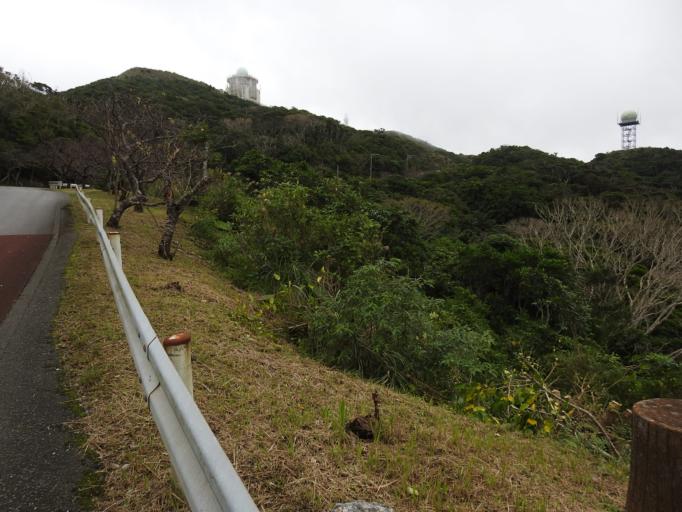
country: JP
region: Okinawa
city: Nago
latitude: 26.6391
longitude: 127.9270
